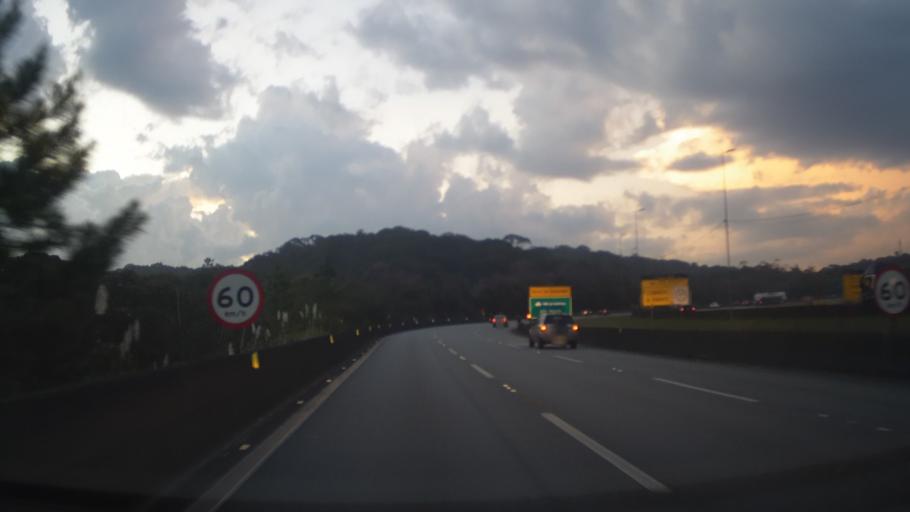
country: BR
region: Sao Paulo
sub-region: Cubatao
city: Cubatao
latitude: -23.8975
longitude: -46.5678
